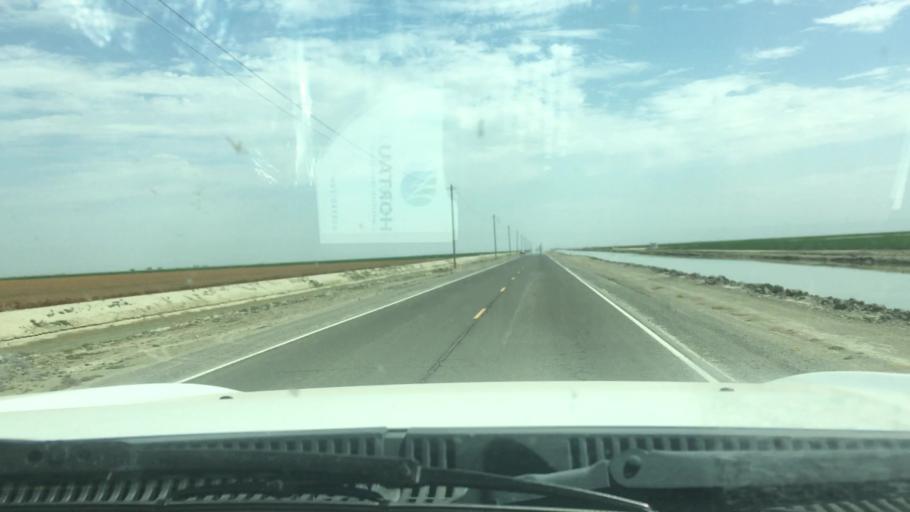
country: US
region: California
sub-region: Tulare County
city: Alpaugh
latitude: 35.9021
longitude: -119.5733
